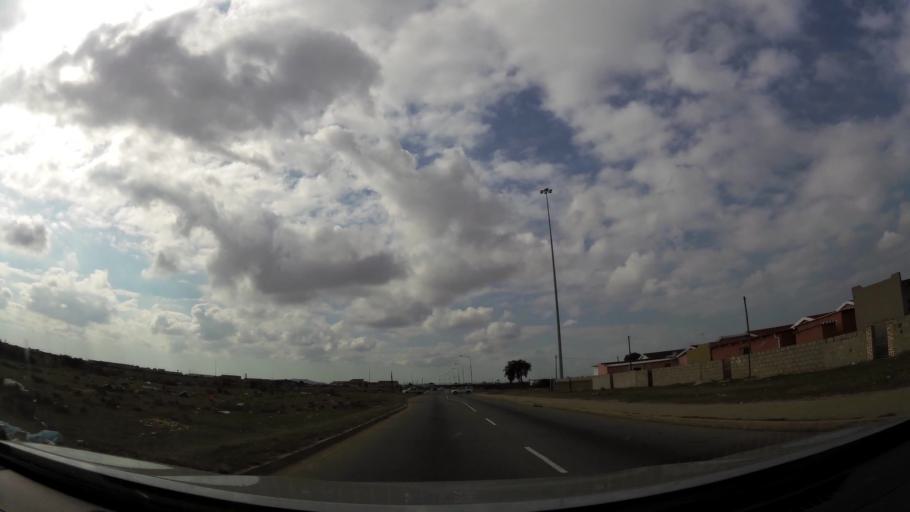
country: ZA
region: Eastern Cape
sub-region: Nelson Mandela Bay Metropolitan Municipality
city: Port Elizabeth
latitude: -33.8181
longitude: 25.5950
